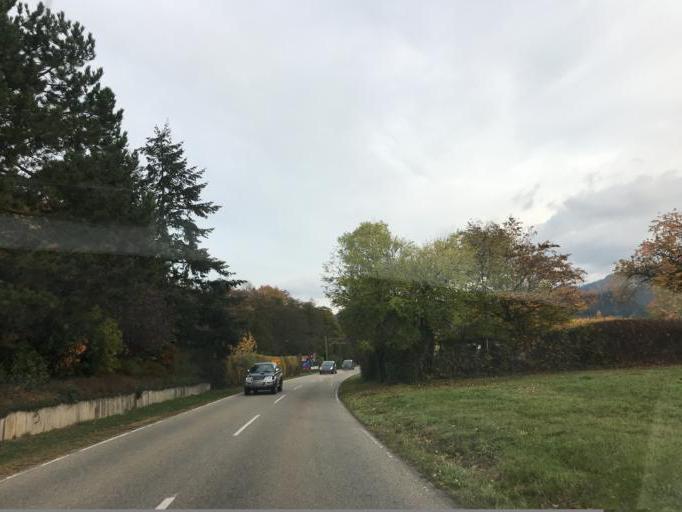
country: DE
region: Baden-Wuerttemberg
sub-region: Freiburg Region
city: Sulzburg
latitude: 47.8754
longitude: 7.7320
